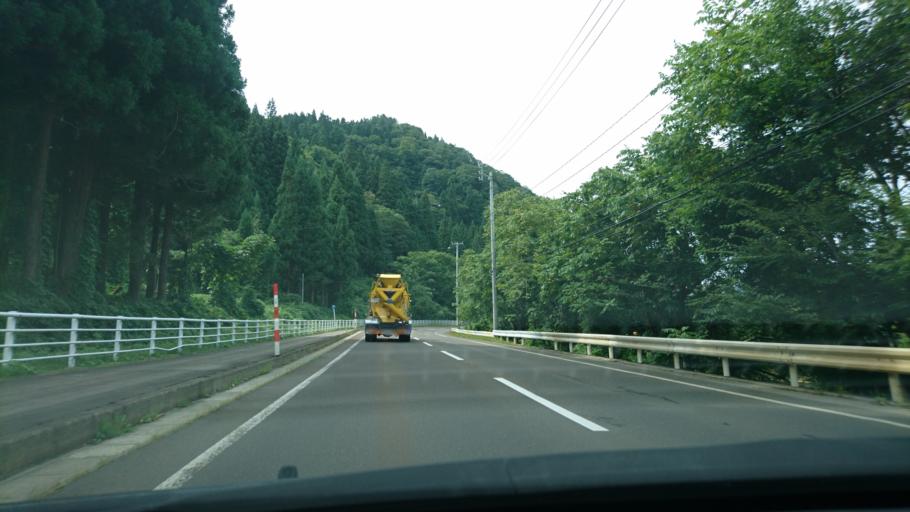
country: JP
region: Akita
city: Yuzawa
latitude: 39.1732
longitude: 140.6702
